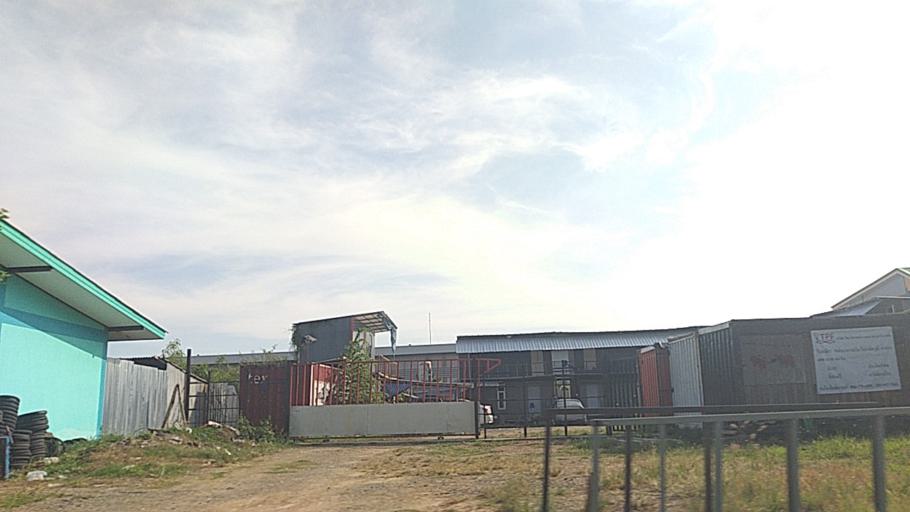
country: TH
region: Pathum Thani
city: Lam Luk Ka
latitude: 13.9613
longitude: 100.7245
